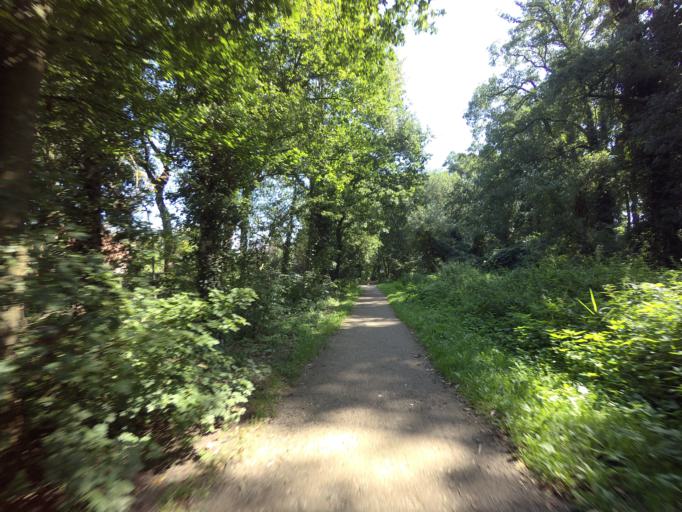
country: NL
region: Gelderland
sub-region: Berkelland
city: Neede
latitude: 52.1275
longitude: 6.6079
